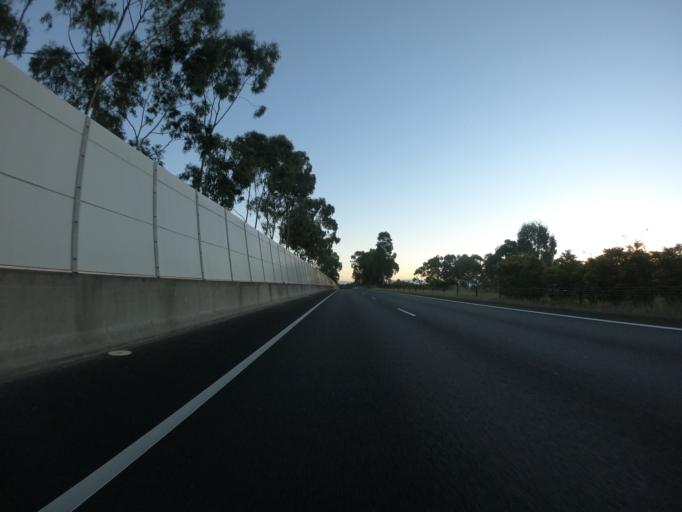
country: AU
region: New South Wales
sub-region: Blacktown
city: Glendenning
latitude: -33.7619
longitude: 150.8466
